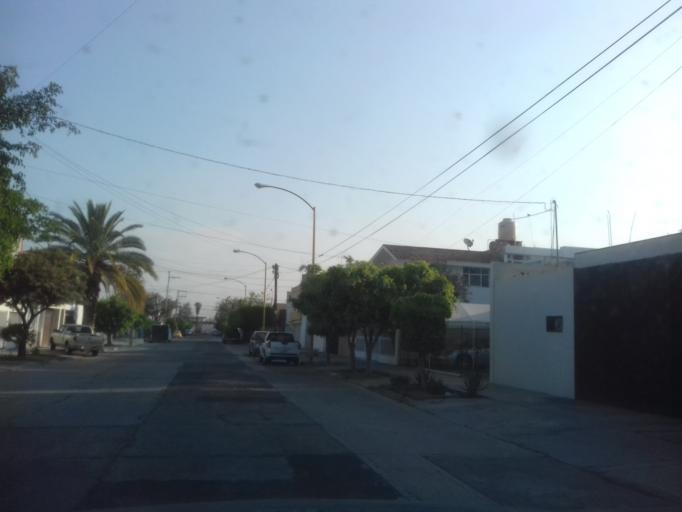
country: MX
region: Aguascalientes
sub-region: Aguascalientes
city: Aguascalientes
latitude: 21.8629
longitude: -102.2913
